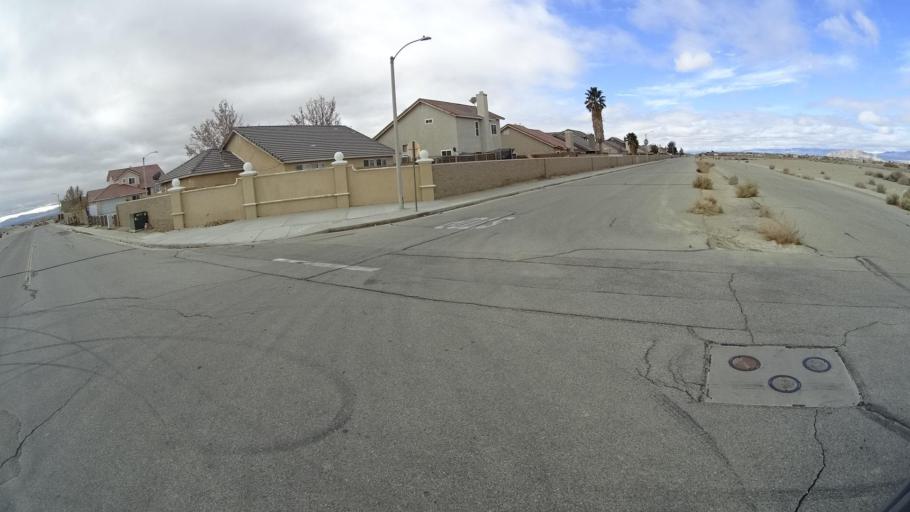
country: US
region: California
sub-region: Kern County
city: Rosamond
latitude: 34.8497
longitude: -118.1759
